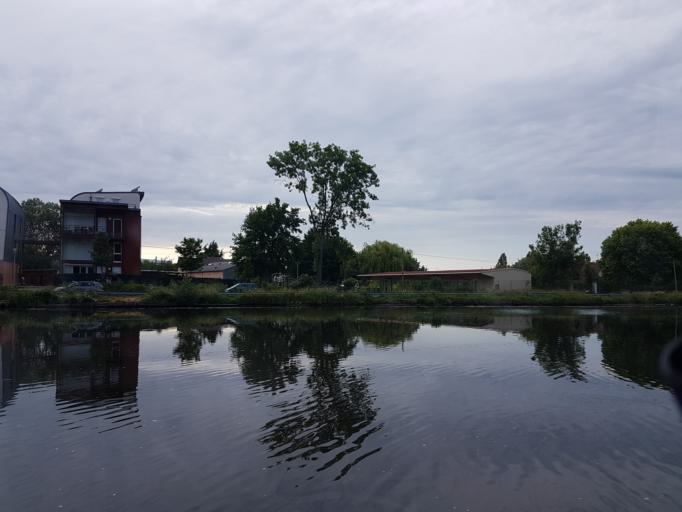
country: FR
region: Bourgogne
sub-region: Departement de l'Yonne
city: Auxerre
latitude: 47.8117
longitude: 3.5785
